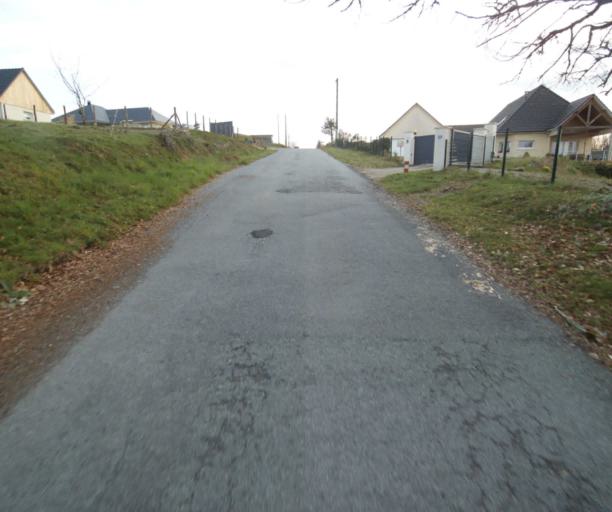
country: FR
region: Limousin
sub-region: Departement de la Correze
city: Correze
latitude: 45.3763
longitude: 1.8820
